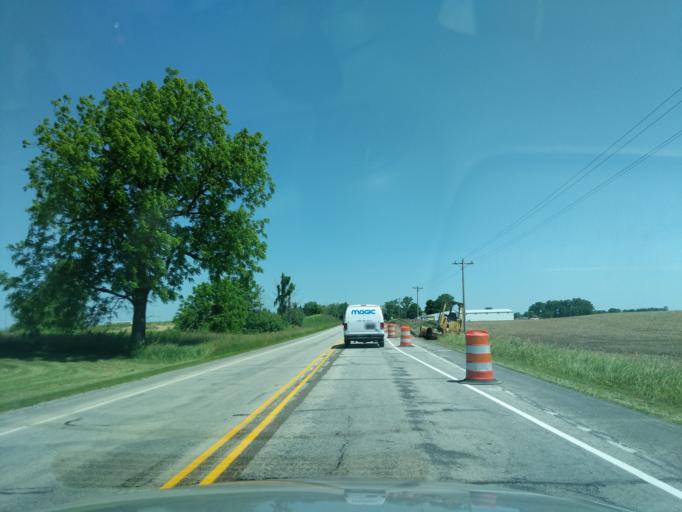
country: US
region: Indiana
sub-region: Whitley County
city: Columbia City
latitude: 41.1339
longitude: -85.4814
